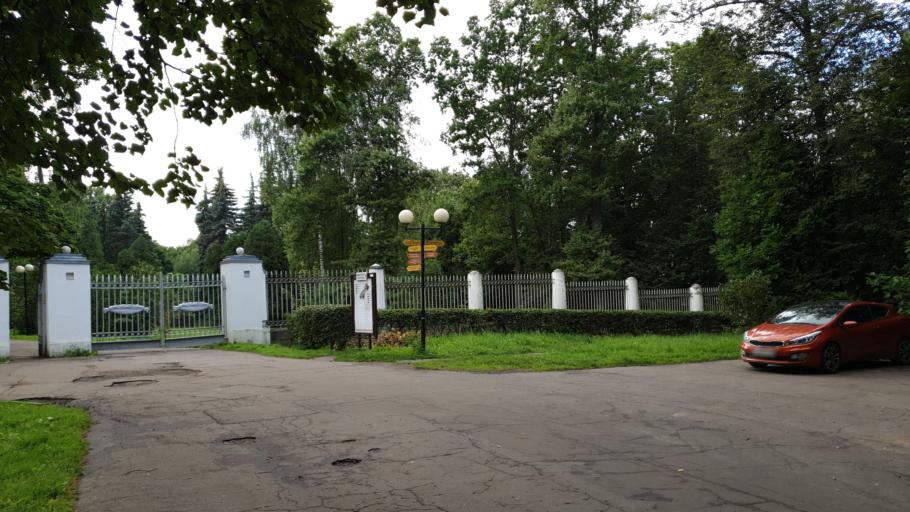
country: RU
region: Moskovskaya
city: Gorki-Leninskiye
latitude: 55.5064
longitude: 37.7665
